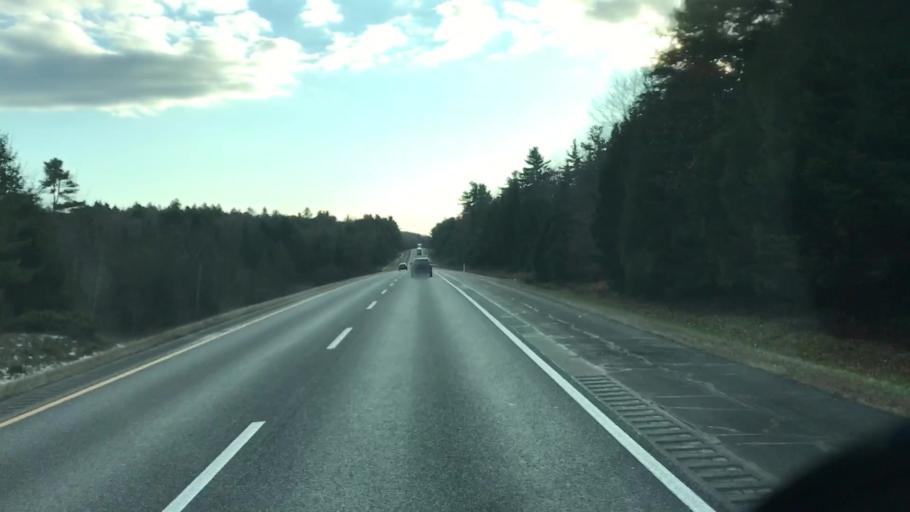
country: US
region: Maine
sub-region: Kennebec County
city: Sidney
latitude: 44.3942
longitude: -69.7574
